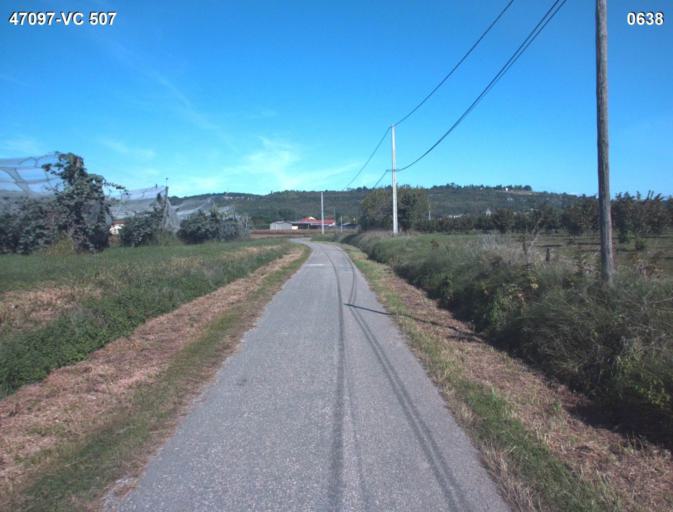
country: FR
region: Aquitaine
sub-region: Departement du Lot-et-Garonne
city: Port-Sainte-Marie
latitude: 44.2413
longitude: 0.3904
